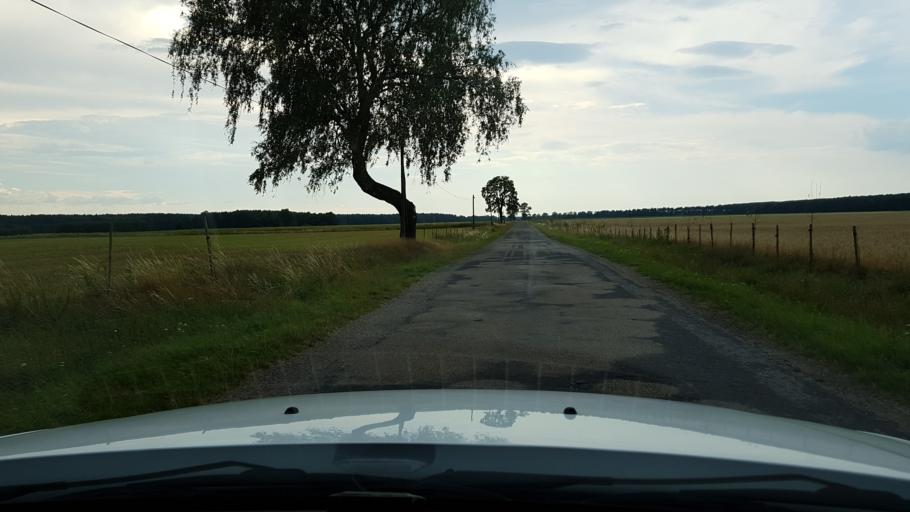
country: PL
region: West Pomeranian Voivodeship
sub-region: Powiat drawski
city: Czaplinek
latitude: 53.4294
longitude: 16.3120
